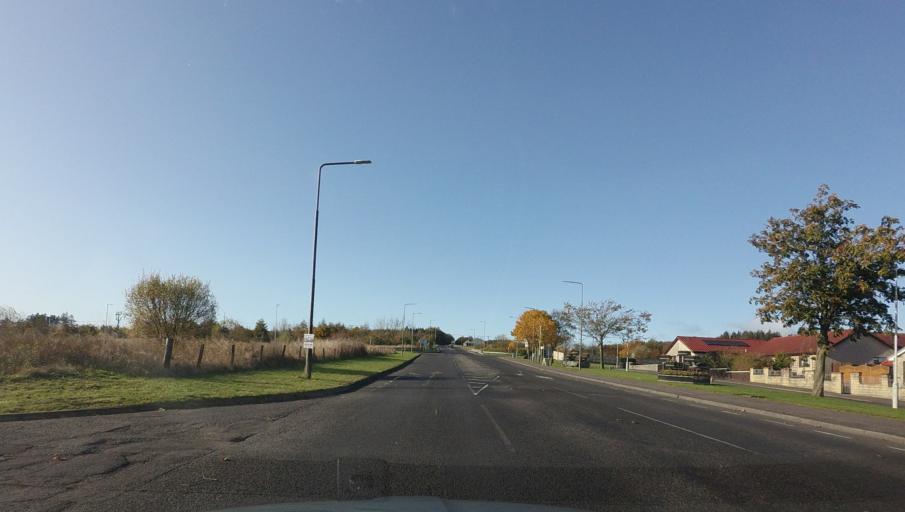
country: GB
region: Scotland
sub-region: Fife
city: Kelty
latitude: 56.1304
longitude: -3.3915
